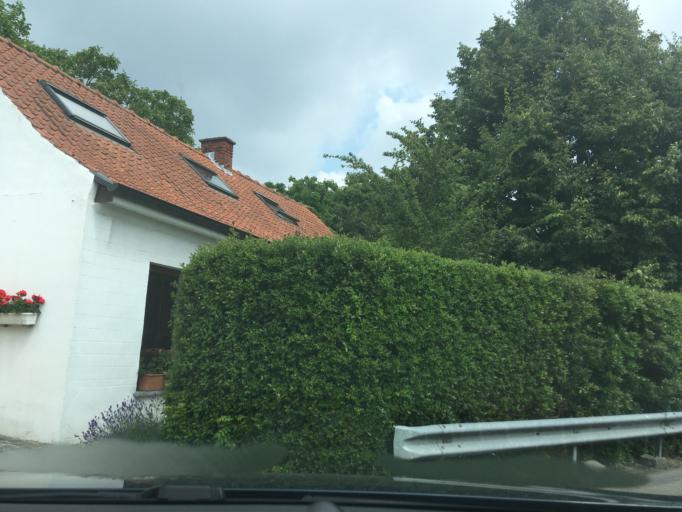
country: BE
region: Flanders
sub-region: Provincie West-Vlaanderen
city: Meulebeke
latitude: 50.9439
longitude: 3.2957
